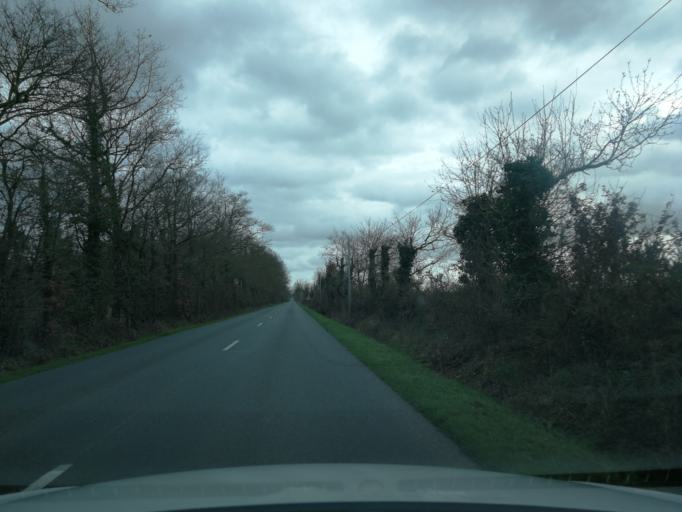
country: FR
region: Pays de la Loire
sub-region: Departement de la Loire-Atlantique
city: Montbert
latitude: 47.0303
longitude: -1.4994
